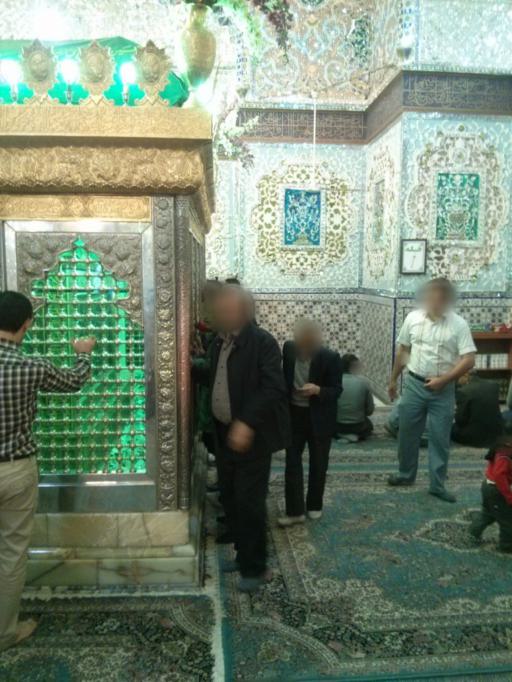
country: IR
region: Qazvin
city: Qazvin
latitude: 36.2572
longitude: 50.0009
